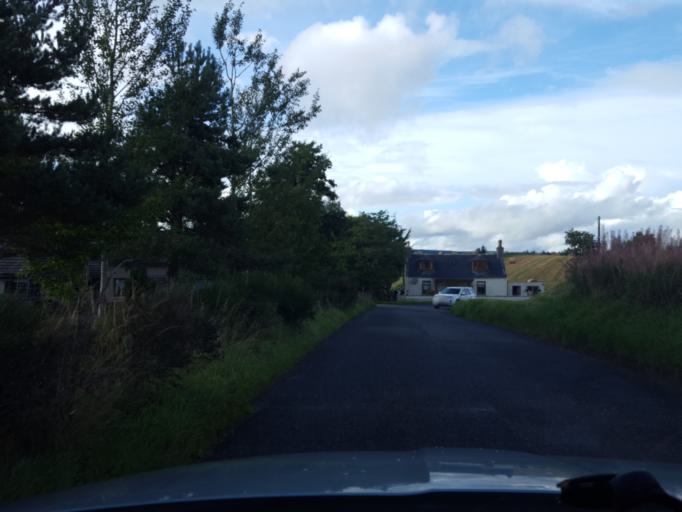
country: GB
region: Scotland
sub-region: Aberdeenshire
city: Alford
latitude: 57.2240
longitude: -2.7132
